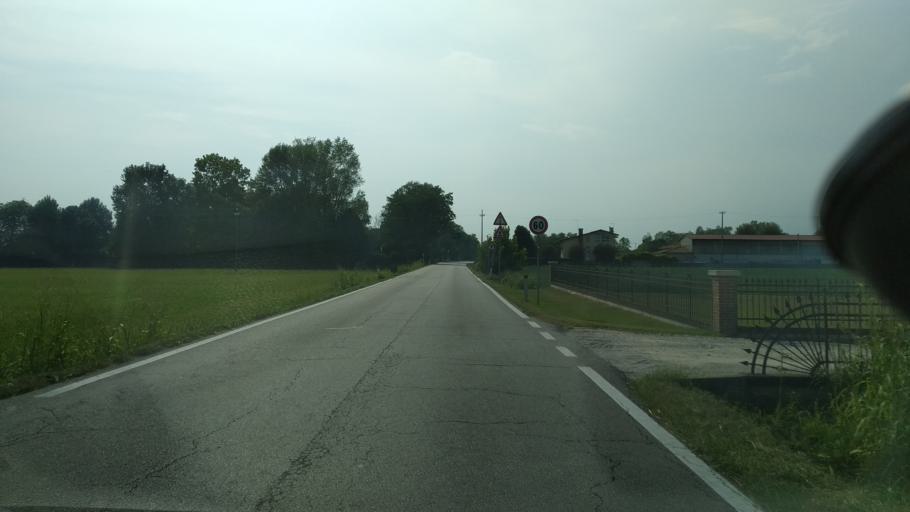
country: IT
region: Veneto
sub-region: Provincia di Padova
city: Fontaniva
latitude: 45.6586
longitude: 11.7295
